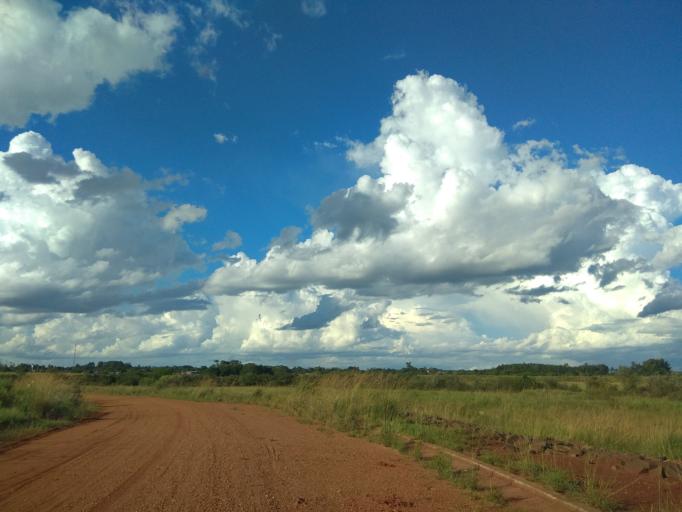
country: AR
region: Misiones
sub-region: Departamento de Candelaria
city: Candelaria
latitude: -27.4865
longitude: -55.7511
